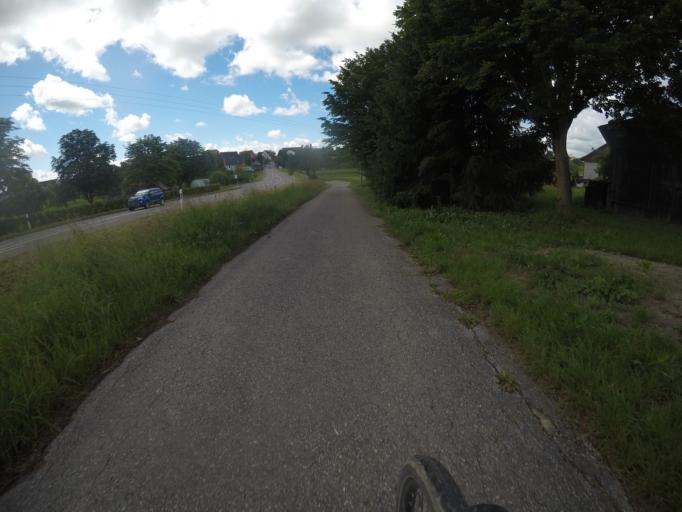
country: DE
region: Baden-Wuerttemberg
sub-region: Regierungsbezirk Stuttgart
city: Motzingen
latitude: 48.5396
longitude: 8.7763
